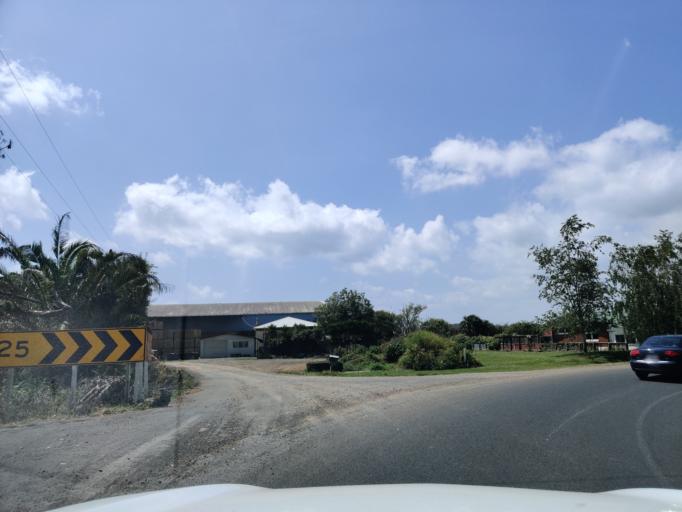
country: NZ
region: Auckland
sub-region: Auckland
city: Pukekohe East
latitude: -37.2397
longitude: 174.9508
